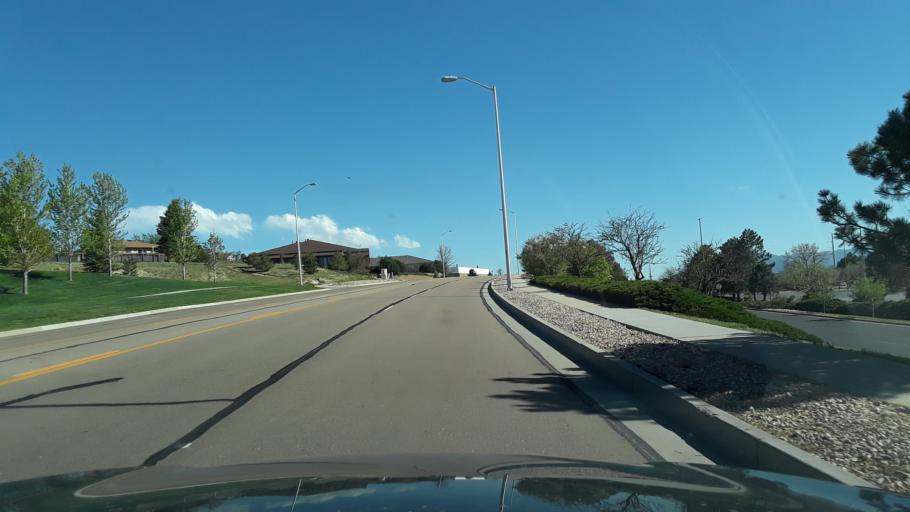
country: US
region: Colorado
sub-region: El Paso County
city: Air Force Academy
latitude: 38.9476
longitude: -104.7917
